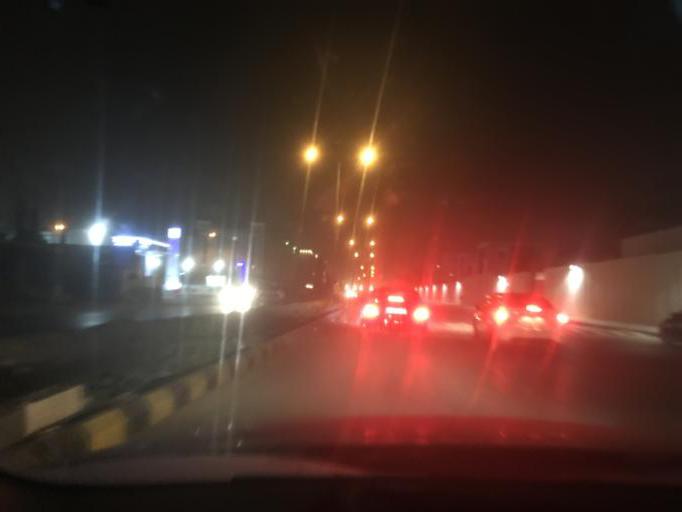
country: SA
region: Ar Riyad
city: Riyadh
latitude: 24.8289
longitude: 46.7351
